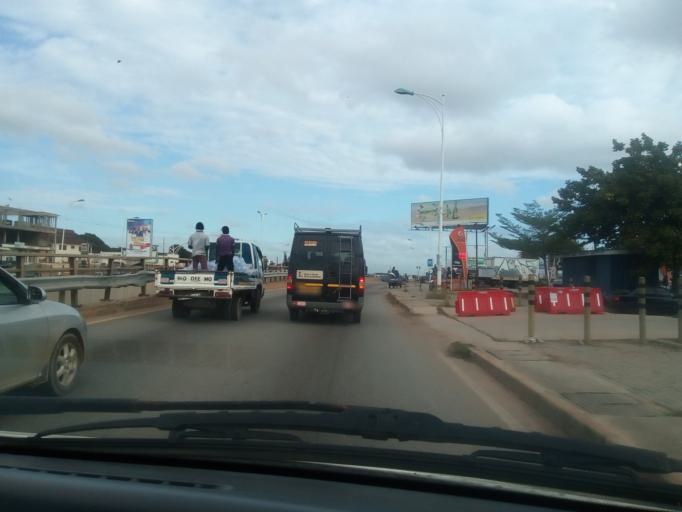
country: GH
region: Greater Accra
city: Dome
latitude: 5.6457
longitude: -0.2475
